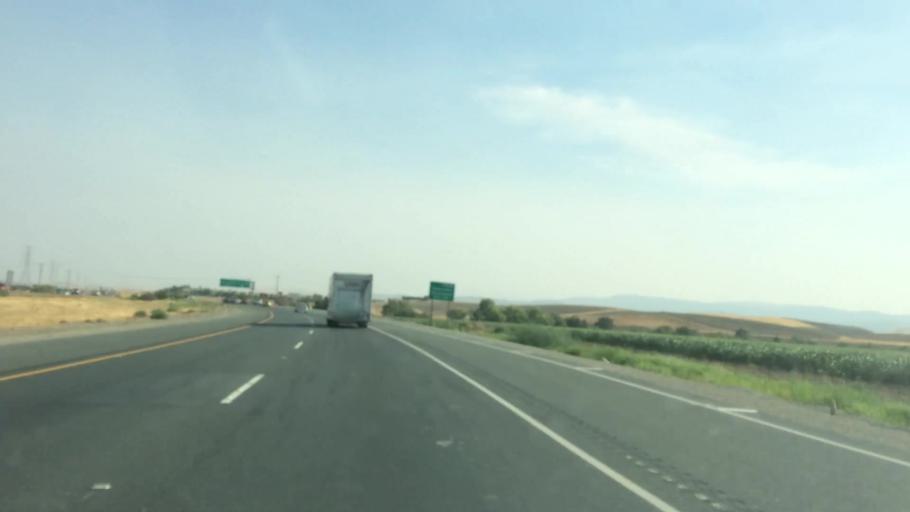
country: US
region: California
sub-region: Contra Costa County
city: Brentwood
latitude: 37.9519
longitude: -121.7450
